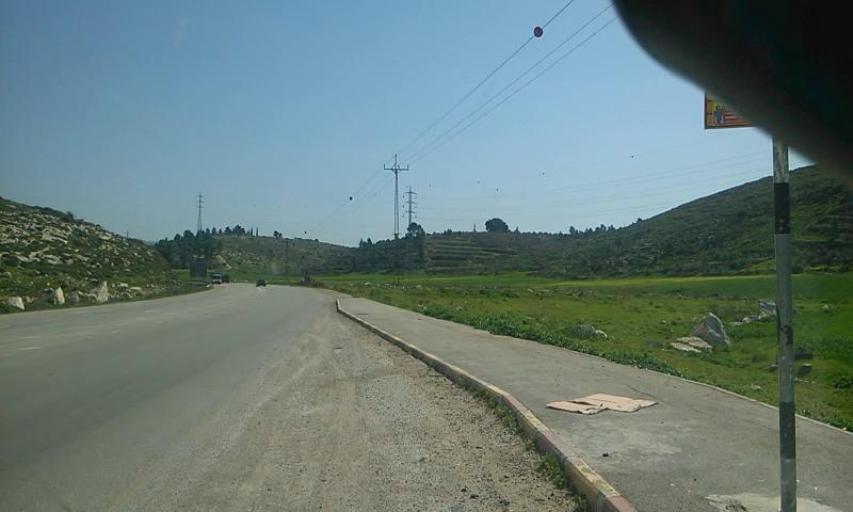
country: PS
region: West Bank
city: Idhna
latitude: 31.5818
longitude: 34.9743
